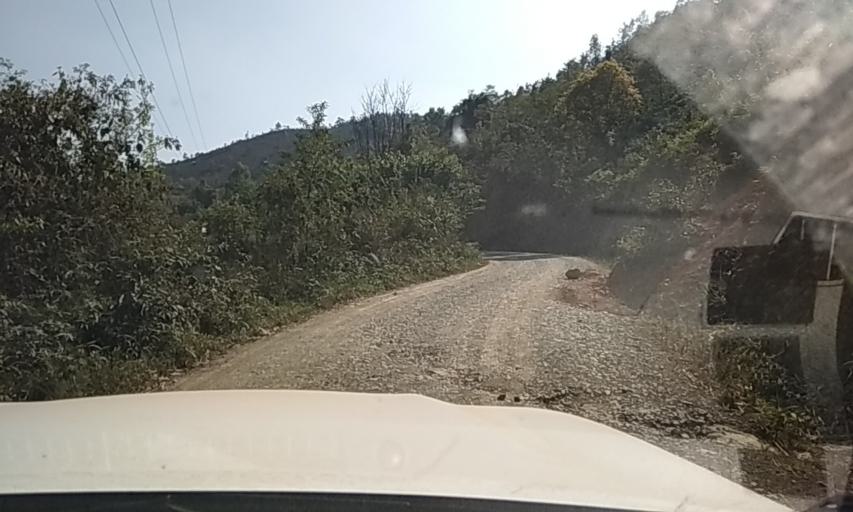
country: LA
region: Phongsali
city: Phongsali
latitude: 21.6566
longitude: 102.0910
